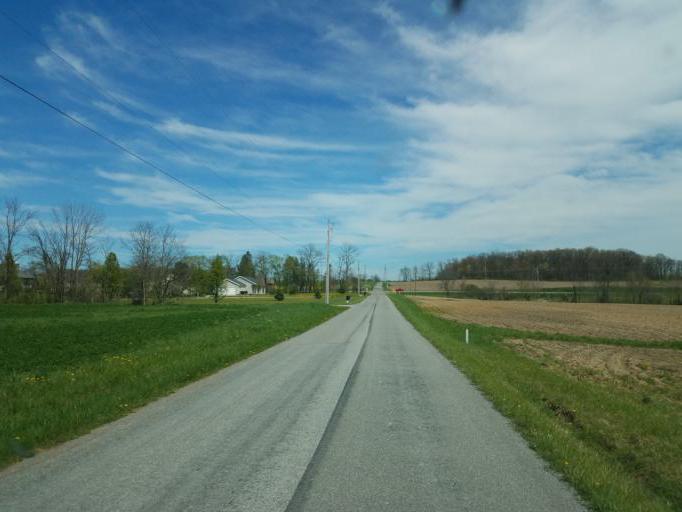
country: US
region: Ohio
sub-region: Huron County
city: Greenwich
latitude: 40.9021
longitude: -82.5040
